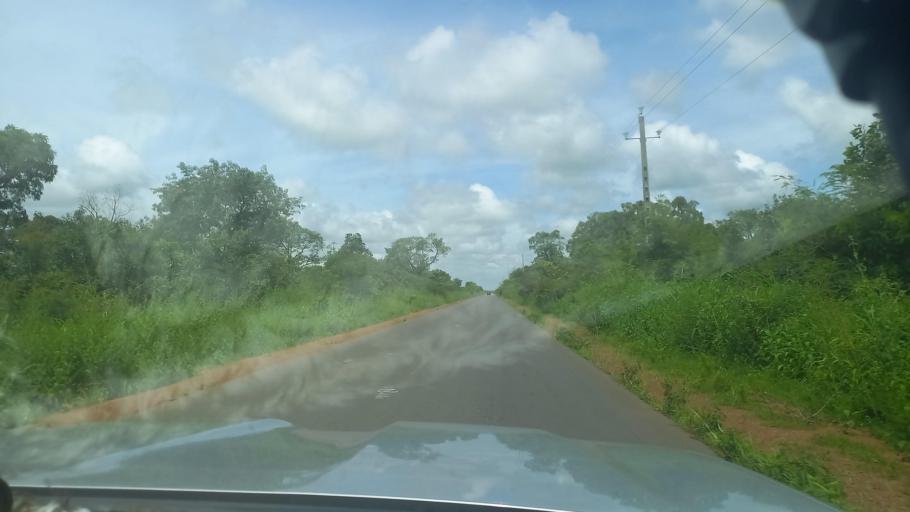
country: GM
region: Lower River
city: Kaiaf
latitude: 13.1848
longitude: -15.5591
